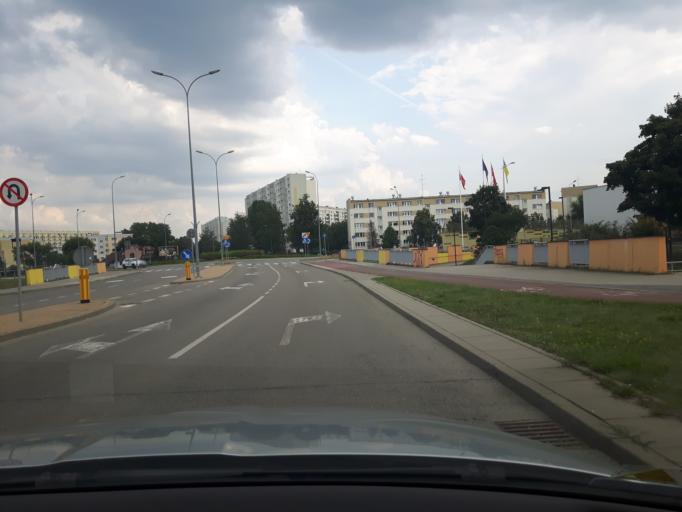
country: PL
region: Pomeranian Voivodeship
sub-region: Sopot
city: Sopot
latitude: 54.4258
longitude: 18.5763
